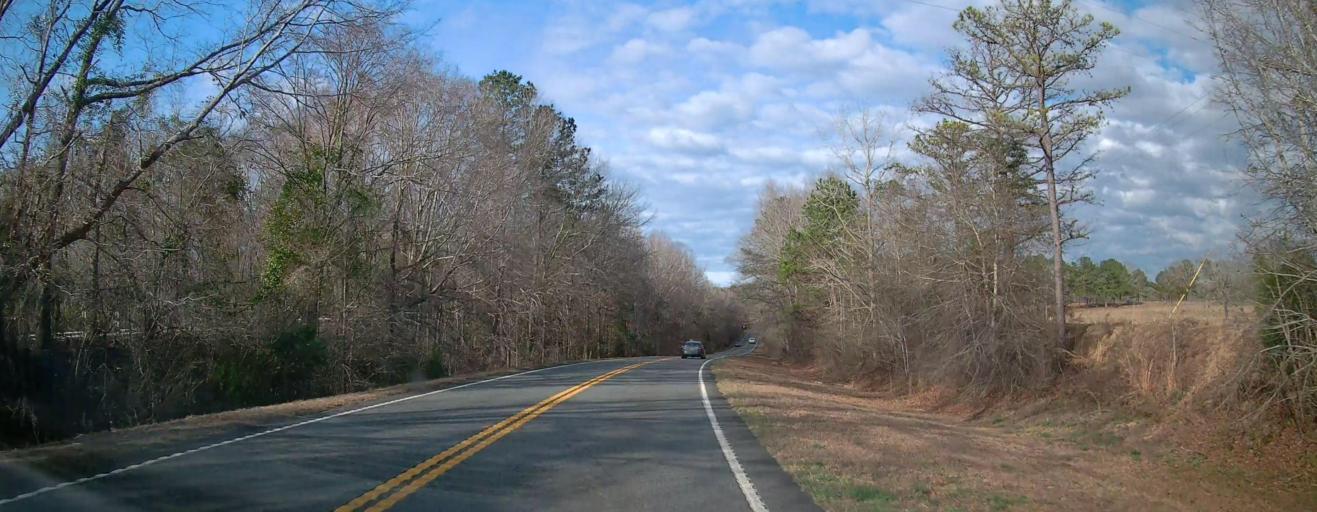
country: US
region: Georgia
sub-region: Talbot County
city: Talbotton
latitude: 32.5385
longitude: -84.6031
